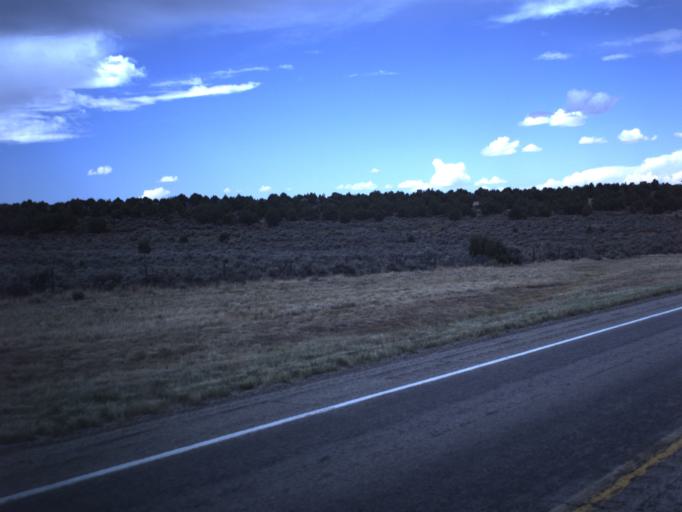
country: US
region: Utah
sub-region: San Juan County
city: Monticello
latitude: 37.9102
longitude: -109.3460
